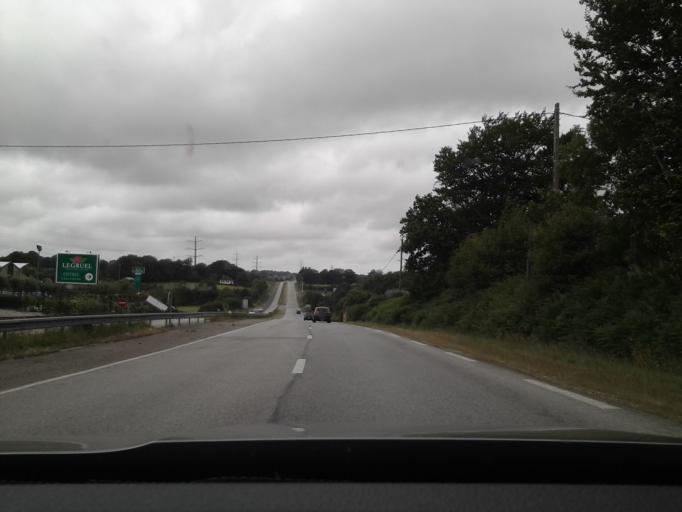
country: FR
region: Lower Normandy
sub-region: Departement de la Manche
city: La Glacerie
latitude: 49.5772
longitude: -1.5809
